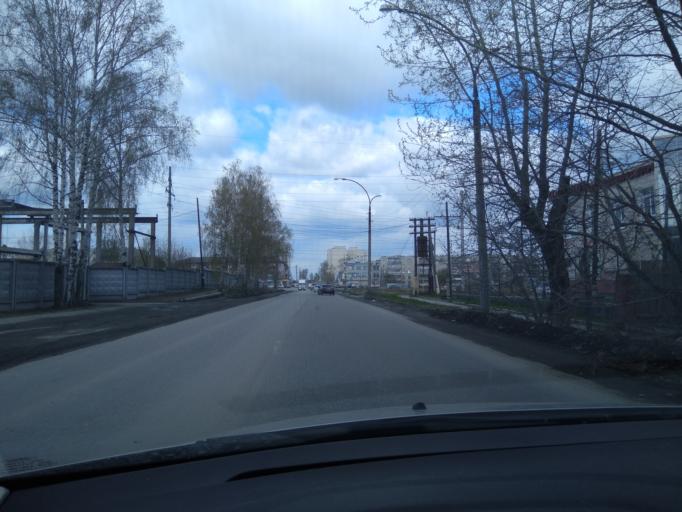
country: RU
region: Sverdlovsk
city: Sredneuralsk
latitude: 56.9911
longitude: 60.4821
